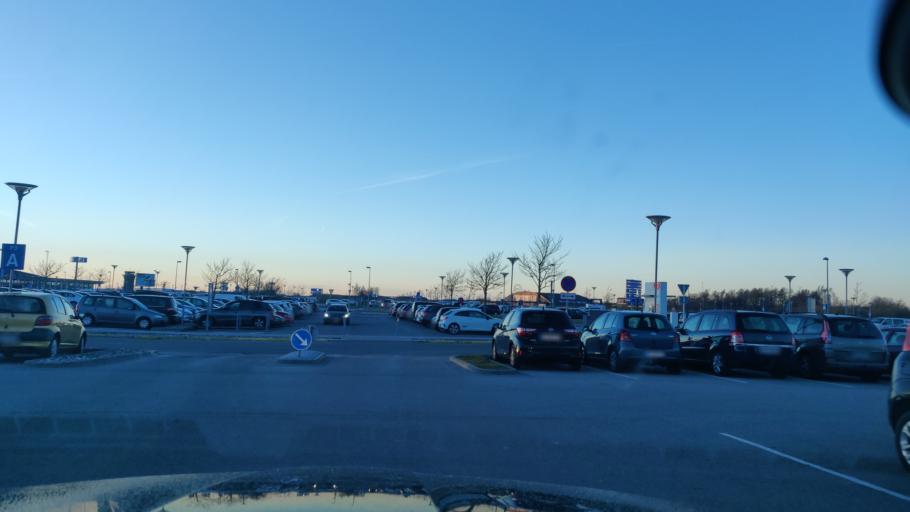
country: DK
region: North Denmark
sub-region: Alborg Kommune
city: Vadum
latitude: 57.0856
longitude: 9.8765
